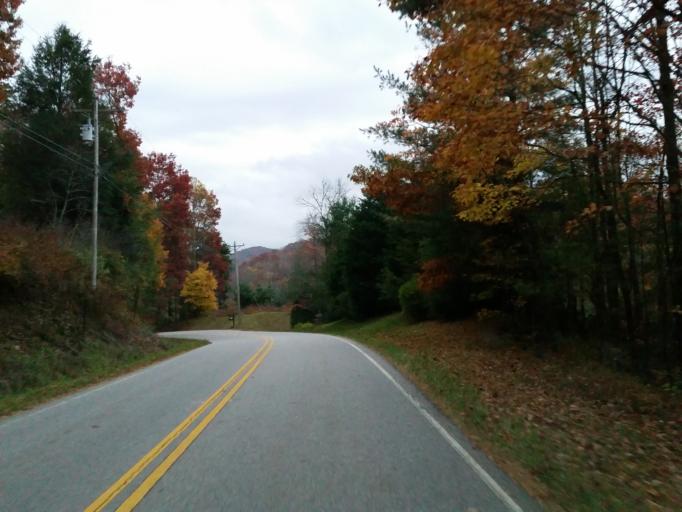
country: US
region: Georgia
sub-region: Lumpkin County
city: Dahlonega
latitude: 34.6949
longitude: -84.0273
